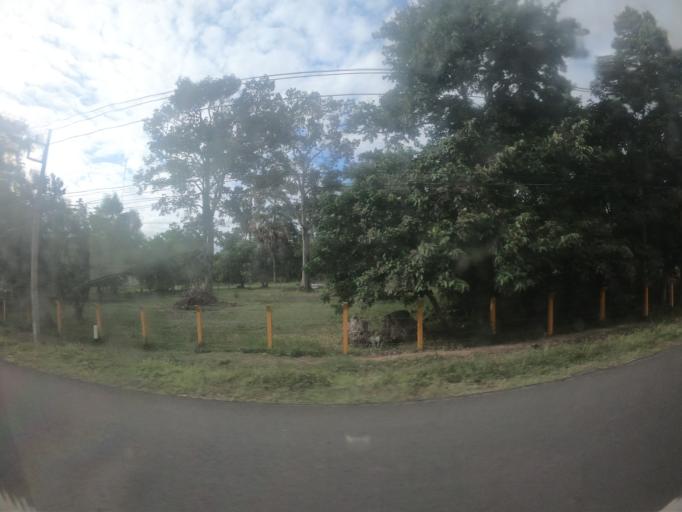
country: TH
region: Surin
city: Prasat
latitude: 14.5909
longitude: 103.4562
